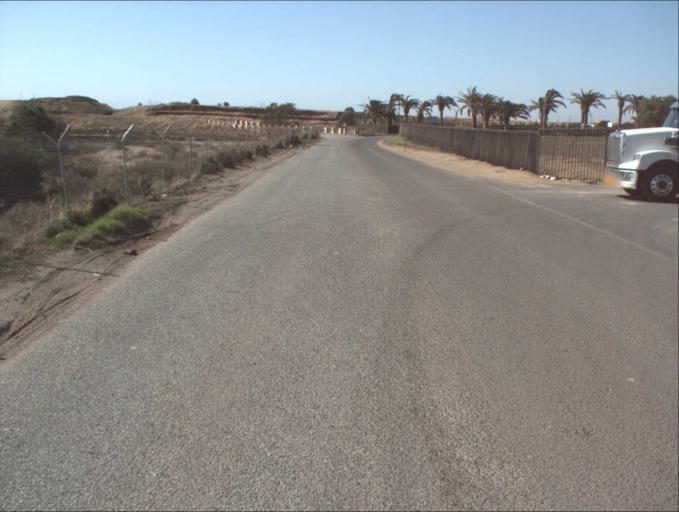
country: AU
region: South Australia
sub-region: Port Adelaide Enfield
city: Alberton
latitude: -34.8312
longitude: 138.5459
